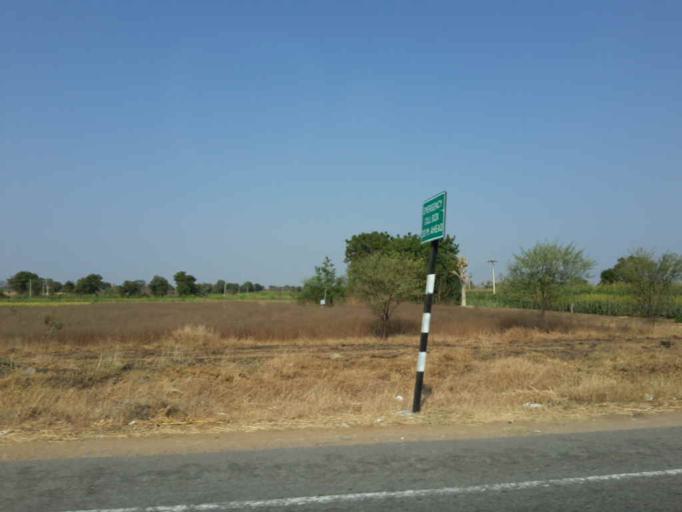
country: IN
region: Telangana
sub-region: Nizamabad District
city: Nizamabad
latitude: 18.7480
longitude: 78.2775
